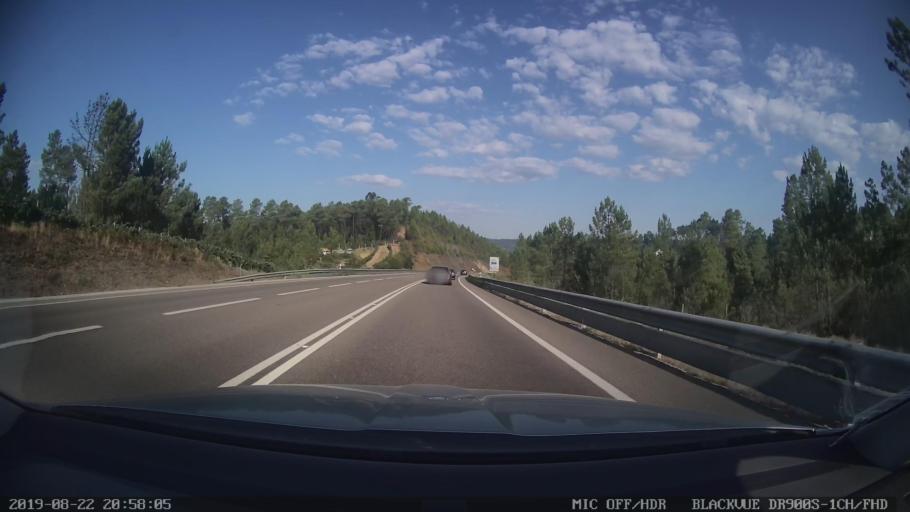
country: PT
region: Castelo Branco
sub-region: Serta
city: Serta
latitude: 39.7975
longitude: -8.0765
